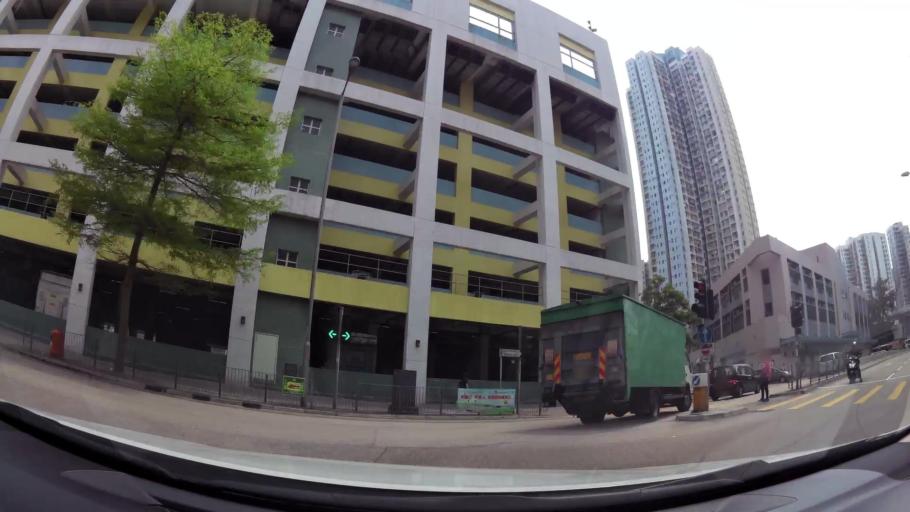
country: HK
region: Wanchai
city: Wan Chai
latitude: 22.2805
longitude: 114.2264
